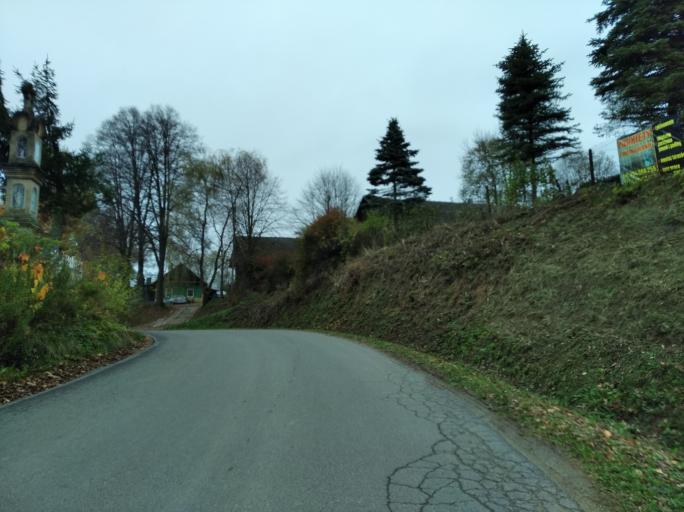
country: PL
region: Subcarpathian Voivodeship
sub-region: Powiat strzyzowski
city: Frysztak
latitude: 49.8293
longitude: 21.6343
